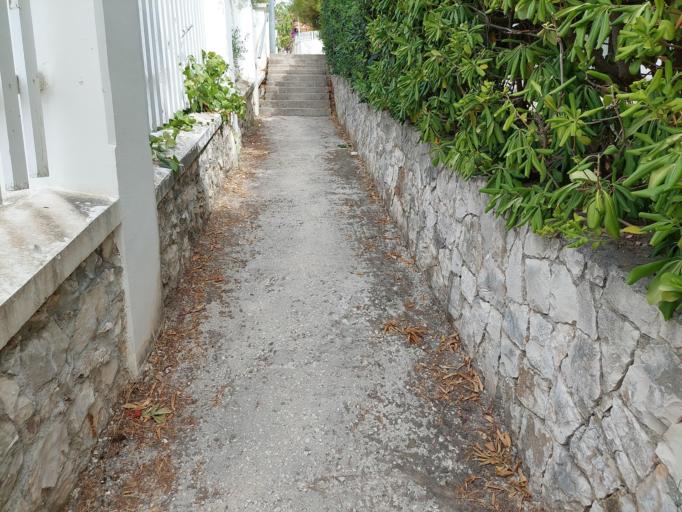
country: HR
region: Splitsko-Dalmatinska
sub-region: Grad Trogir
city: Trogir
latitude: 43.4891
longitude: 16.2792
